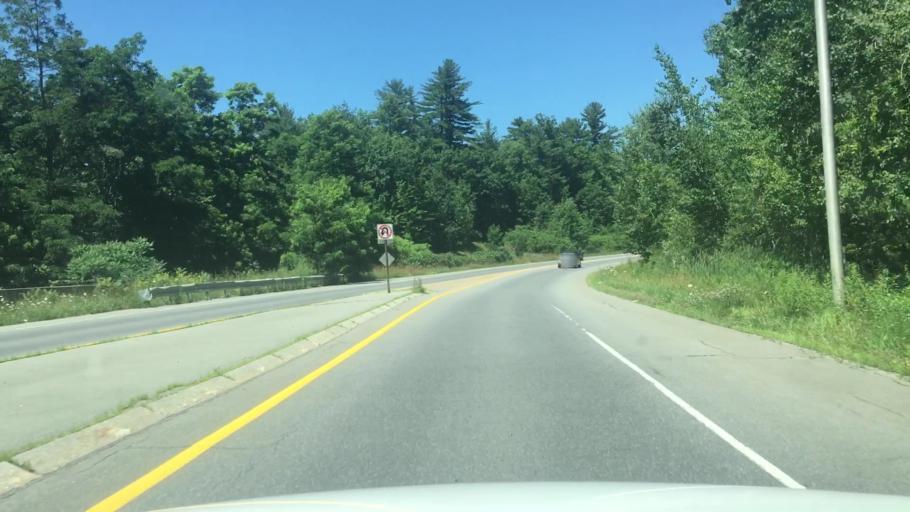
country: US
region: Maine
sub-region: Kennebec County
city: Waterville
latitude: 44.5341
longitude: -69.6503
